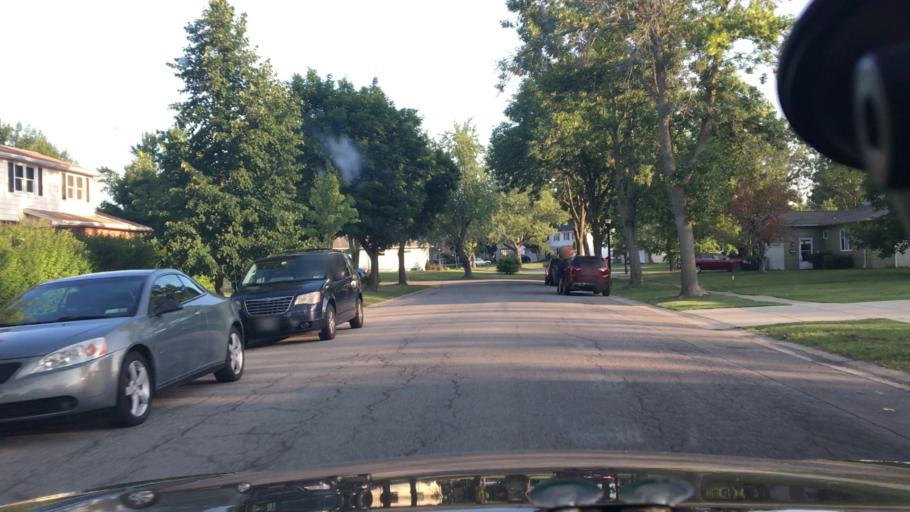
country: US
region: New York
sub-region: Erie County
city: Amherst
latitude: 43.0075
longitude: -78.7621
